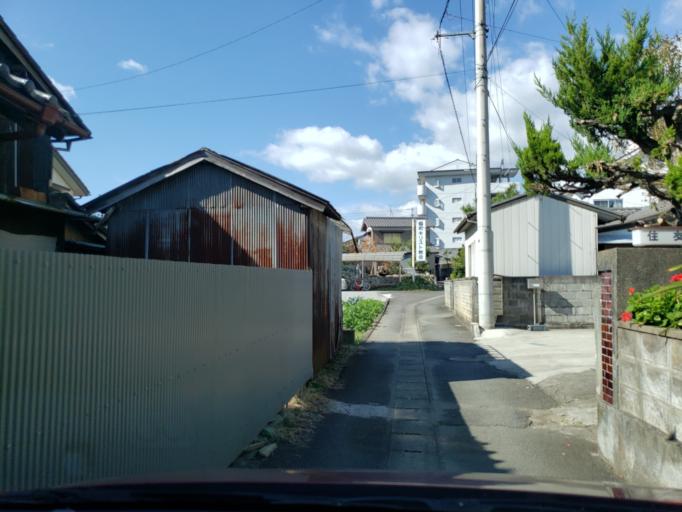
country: JP
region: Tokushima
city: Wakimachi
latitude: 34.0670
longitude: 134.1546
